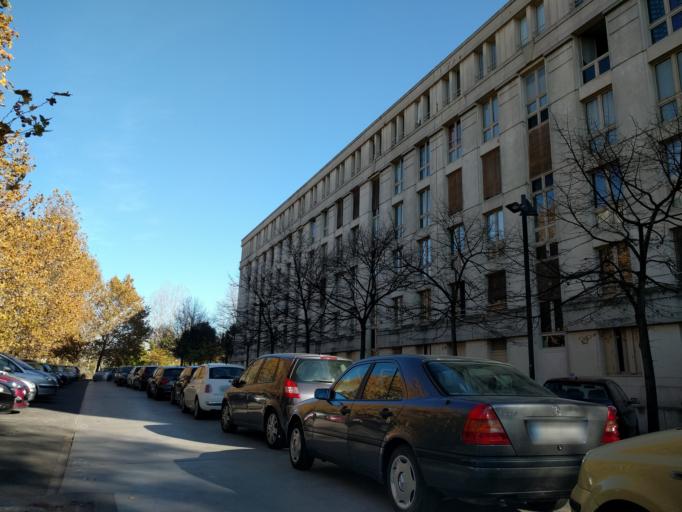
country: FR
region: Languedoc-Roussillon
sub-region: Departement de l'Herault
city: Montpellier
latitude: 43.6105
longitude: 3.8956
